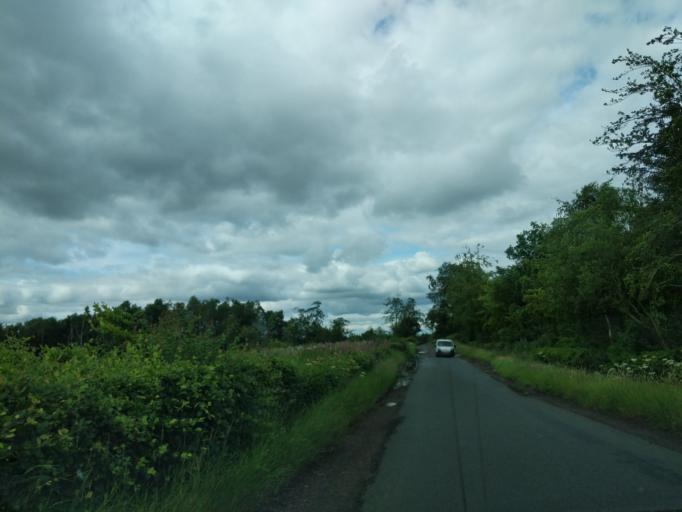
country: GB
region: Scotland
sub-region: South Lanarkshire
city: Larkhall
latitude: 55.7091
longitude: -3.9424
